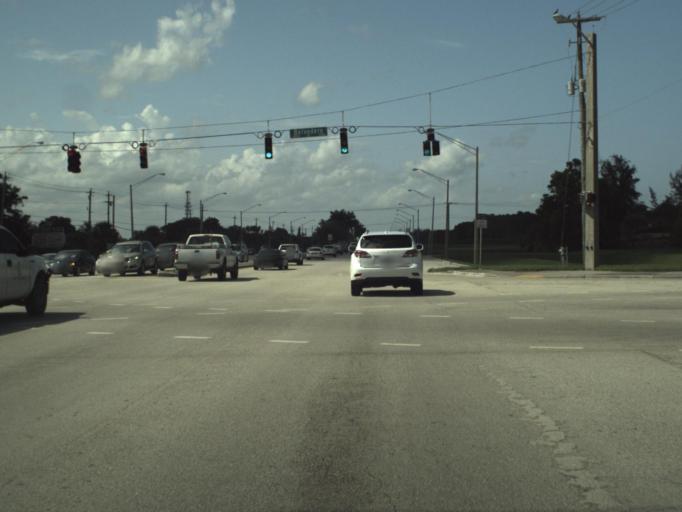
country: US
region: Florida
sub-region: Palm Beach County
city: Royal Palm Beach
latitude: 26.6913
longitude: -80.2015
